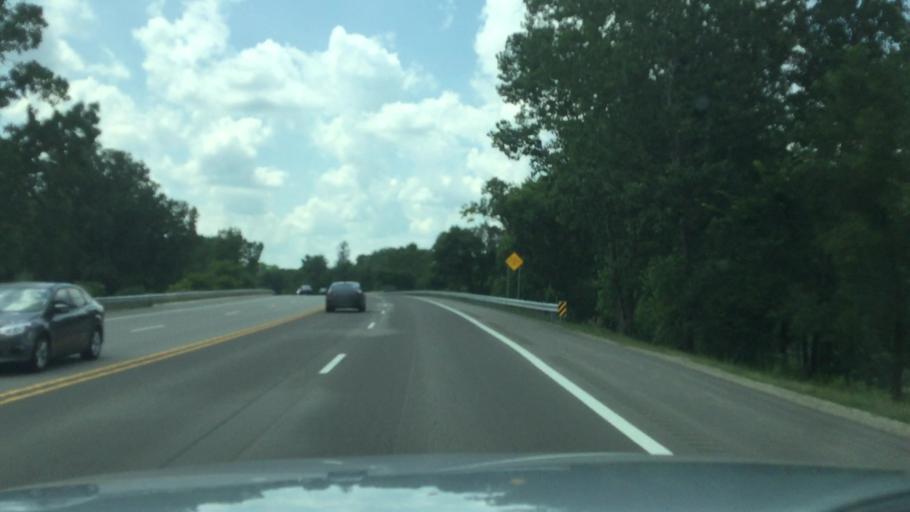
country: US
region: Michigan
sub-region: Washtenaw County
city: Ypsilanti
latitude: 42.2468
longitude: -83.5571
